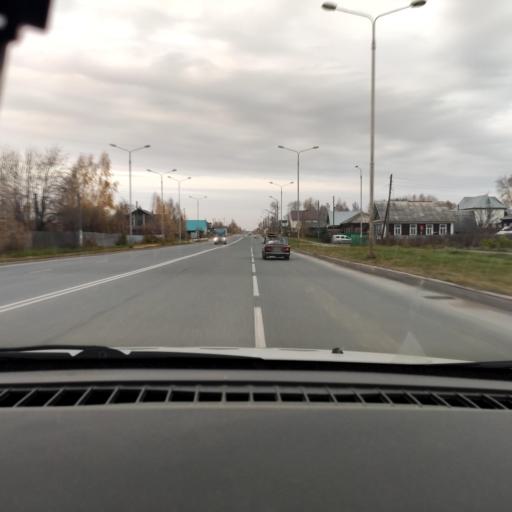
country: RU
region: Perm
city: Polazna
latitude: 58.1122
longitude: 56.3998
